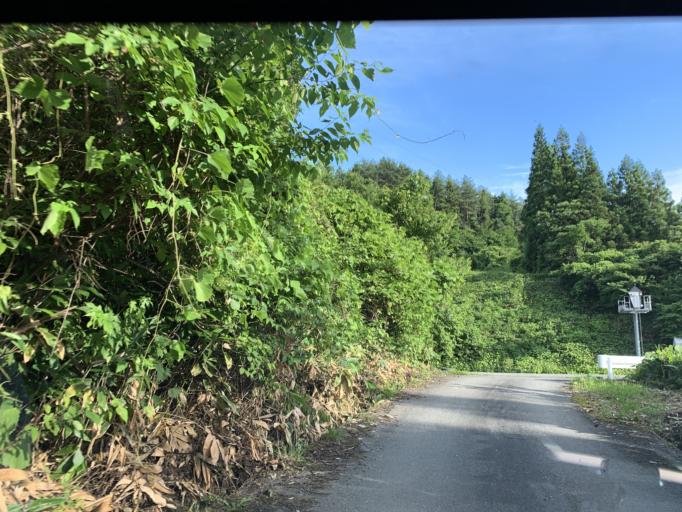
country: JP
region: Iwate
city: Ichinoseki
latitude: 38.9012
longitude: 140.9247
